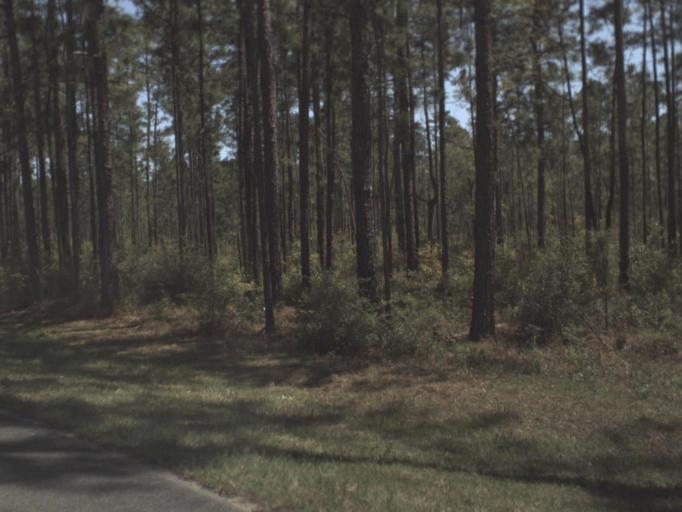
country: US
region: Florida
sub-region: Okaloosa County
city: Crestview
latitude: 30.8523
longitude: -86.8169
